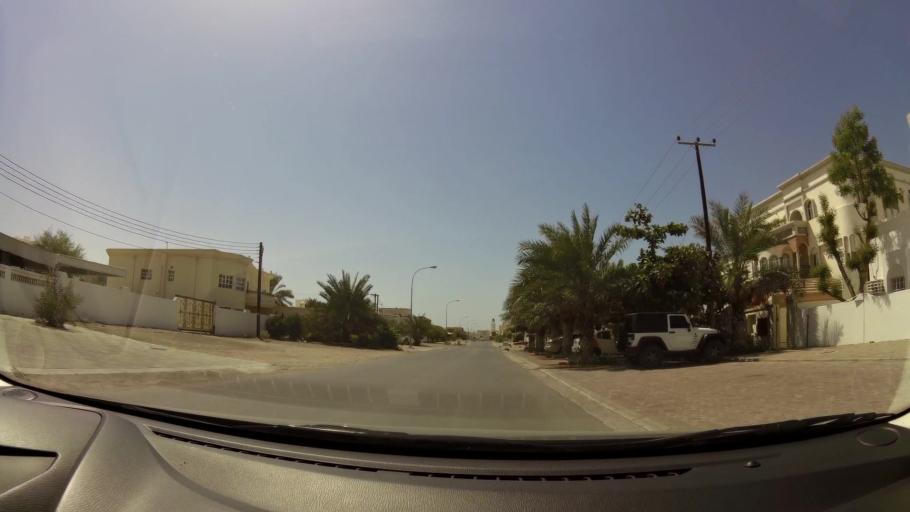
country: OM
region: Muhafazat Masqat
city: As Sib al Jadidah
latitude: 23.6214
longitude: 58.2209
